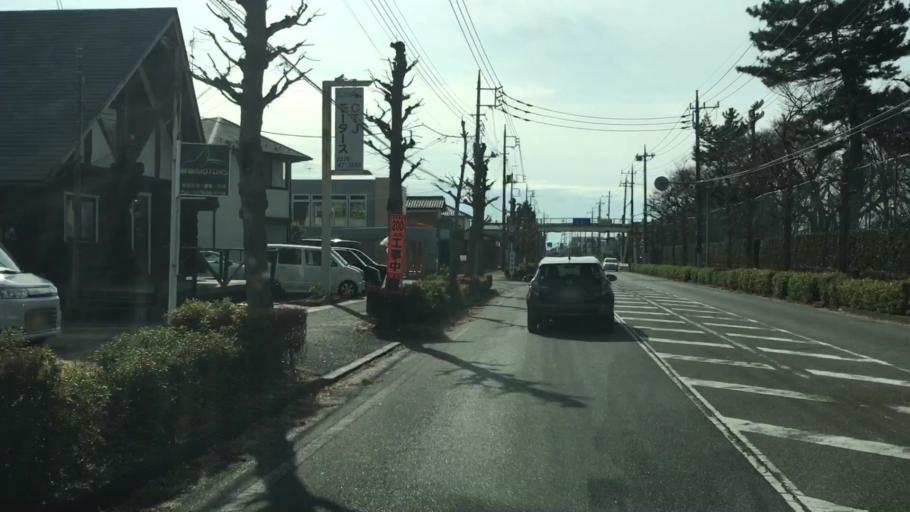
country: JP
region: Saitama
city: Menuma
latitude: 36.2449
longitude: 139.4091
